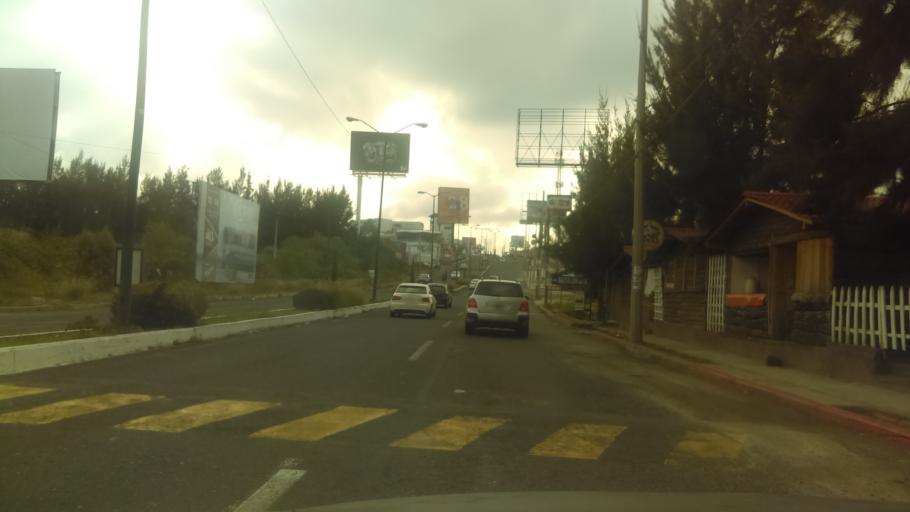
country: MX
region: Michoacan
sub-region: Morelia
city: Montana Monarca (Punta Altozano)
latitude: 19.6710
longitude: -101.1722
